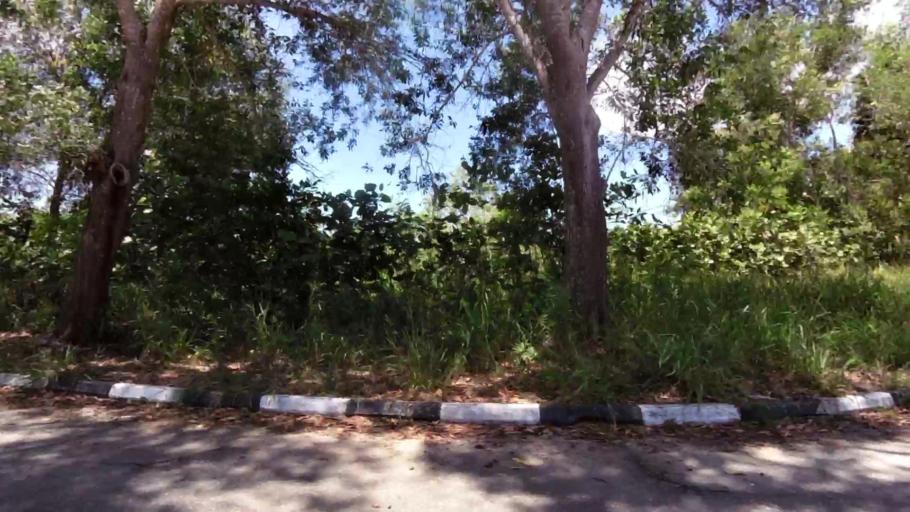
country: BN
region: Brunei and Muara
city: Bandar Seri Begawan
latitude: 4.9242
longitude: 114.9675
